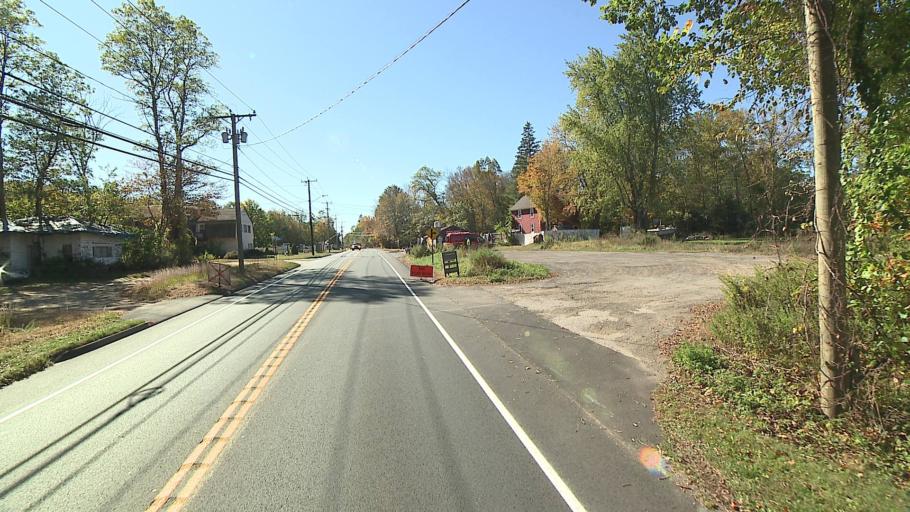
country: US
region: Connecticut
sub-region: Middlesex County
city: Lake Pocotopaug
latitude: 41.6015
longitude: -72.4870
